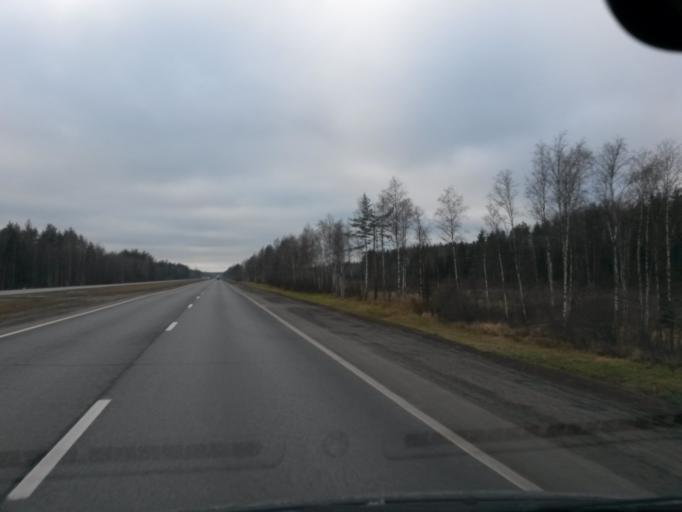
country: RU
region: Jaroslavl
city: Krasnyye Tkachi
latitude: 57.4875
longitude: 39.7783
